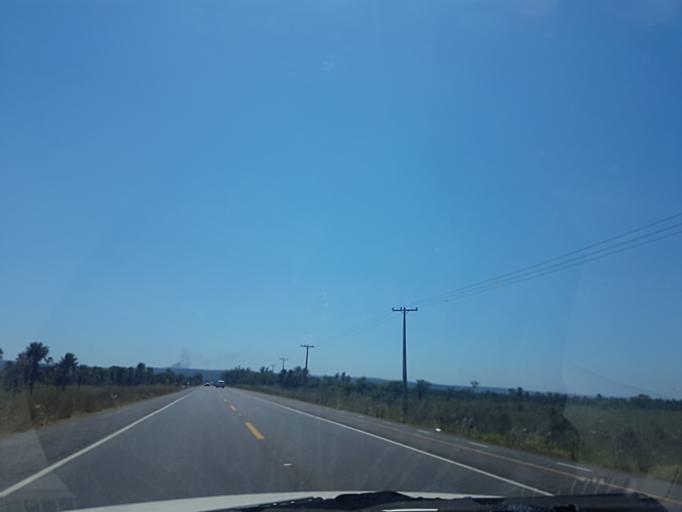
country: PY
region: Cordillera
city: Emboscada
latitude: -25.2089
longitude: -57.3952
